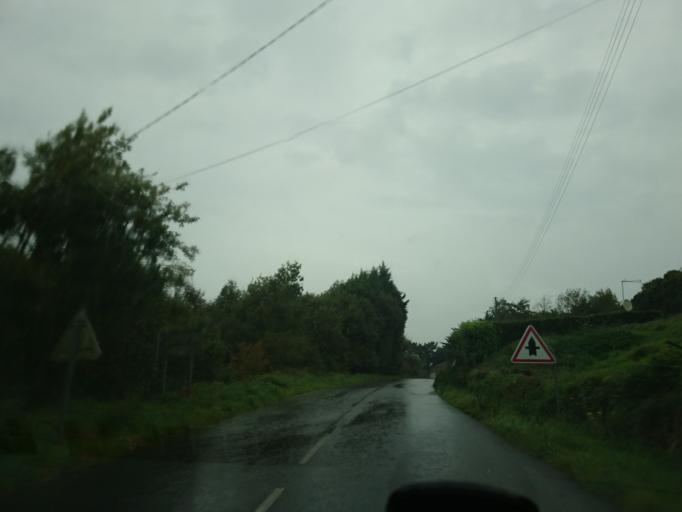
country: FR
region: Brittany
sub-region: Departement du Finistere
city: Plouguerneau
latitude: 48.5973
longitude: -4.5104
